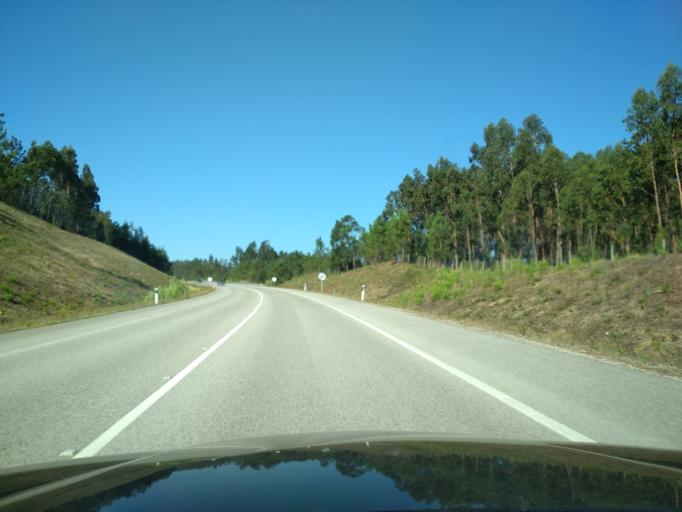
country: PT
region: Leiria
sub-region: Pombal
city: Lourical
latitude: 39.9883
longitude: -8.7423
